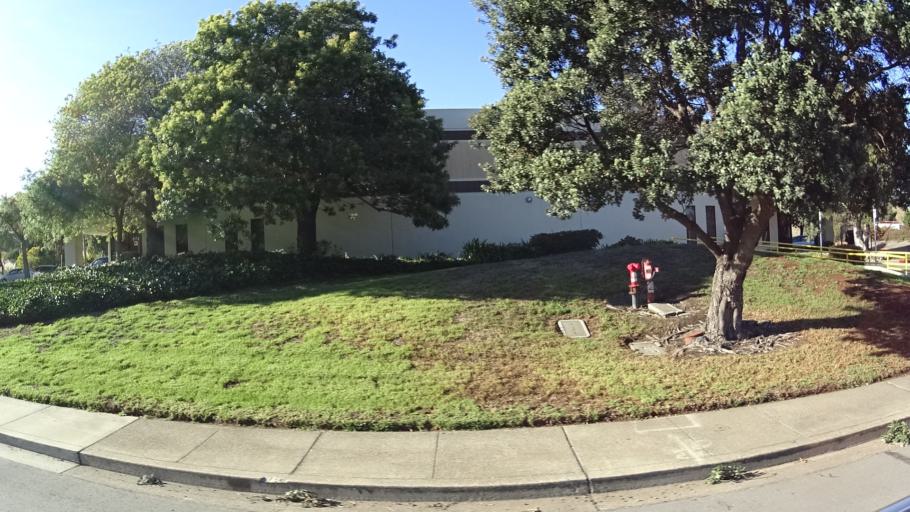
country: US
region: California
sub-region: San Mateo County
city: South San Francisco
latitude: 37.6589
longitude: -122.3857
